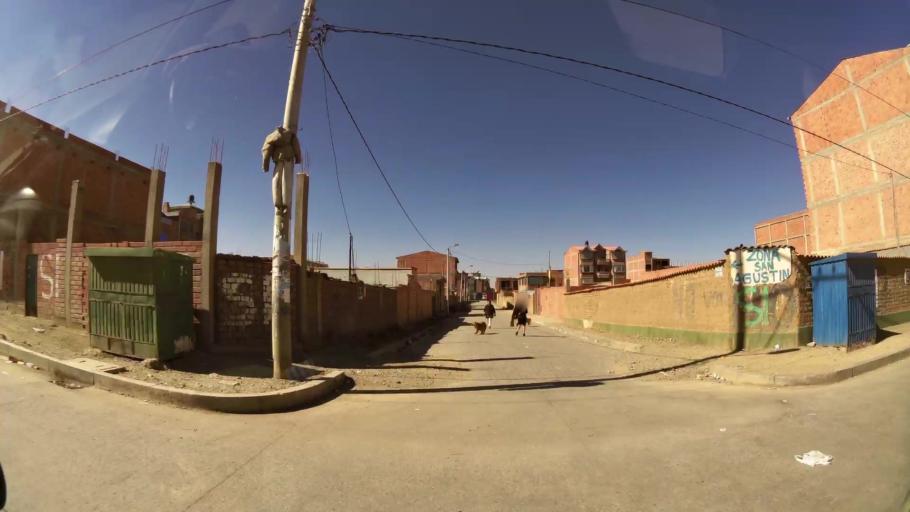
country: BO
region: La Paz
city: La Paz
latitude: -16.5374
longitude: -68.2233
